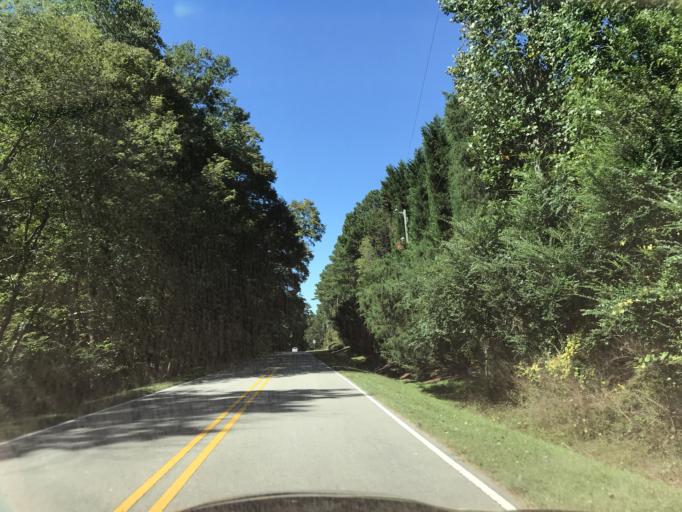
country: US
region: North Carolina
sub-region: Wake County
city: Wake Forest
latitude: 35.9477
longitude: -78.6037
